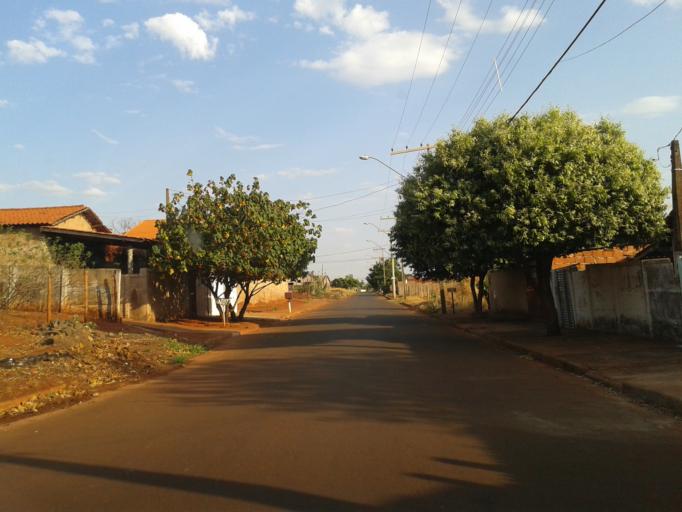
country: BR
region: Minas Gerais
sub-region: Ituiutaba
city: Ituiutaba
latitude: -18.9917
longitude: -49.4376
